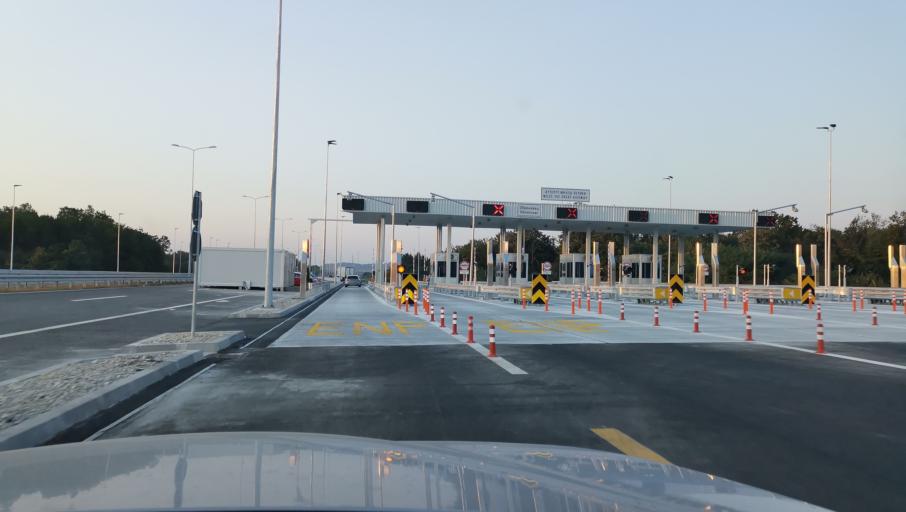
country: RS
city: Stubline
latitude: 44.5708
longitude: 20.1901
